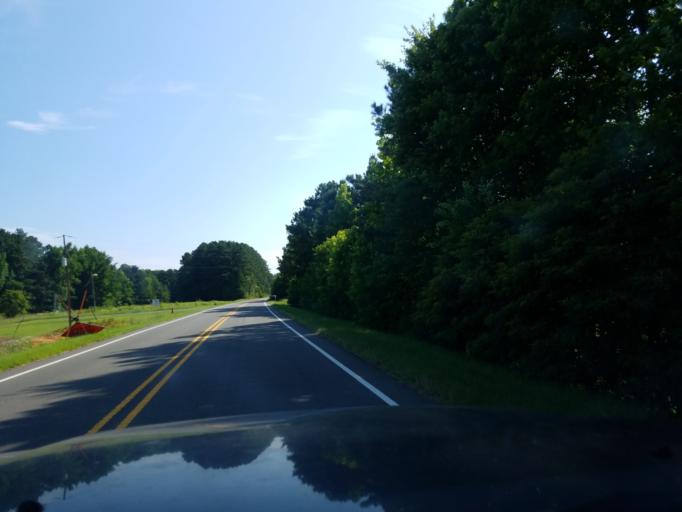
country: US
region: North Carolina
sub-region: Granville County
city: Oxford
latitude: 36.2759
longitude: -78.6427
